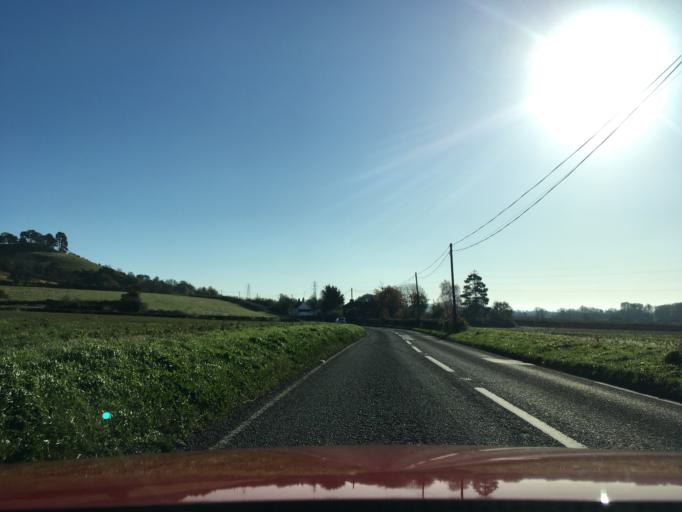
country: GB
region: England
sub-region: Somerset
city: Langport
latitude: 51.0544
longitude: -2.8449
